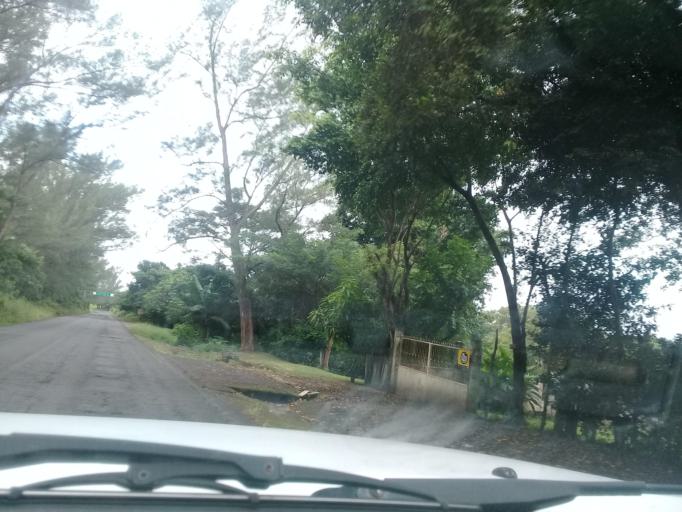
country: MX
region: Veracruz
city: Santiago Tuxtla
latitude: 18.4642
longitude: -95.2851
